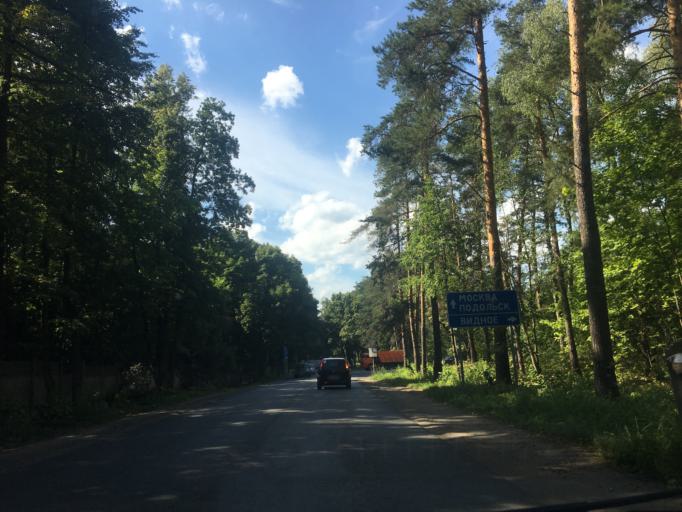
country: RU
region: Moscow
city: Zagor'ye
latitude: 55.5281
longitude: 37.6618
